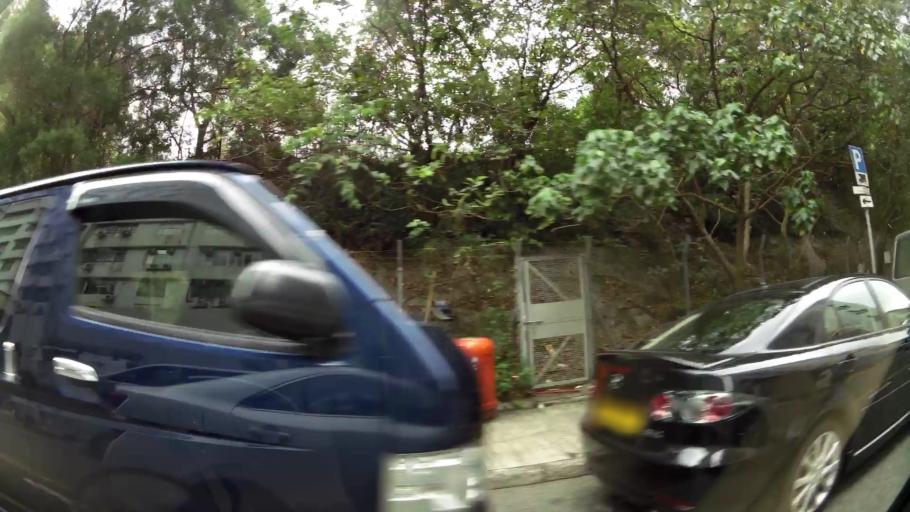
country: HK
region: Sha Tin
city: Sha Tin
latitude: 22.3993
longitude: 114.1945
